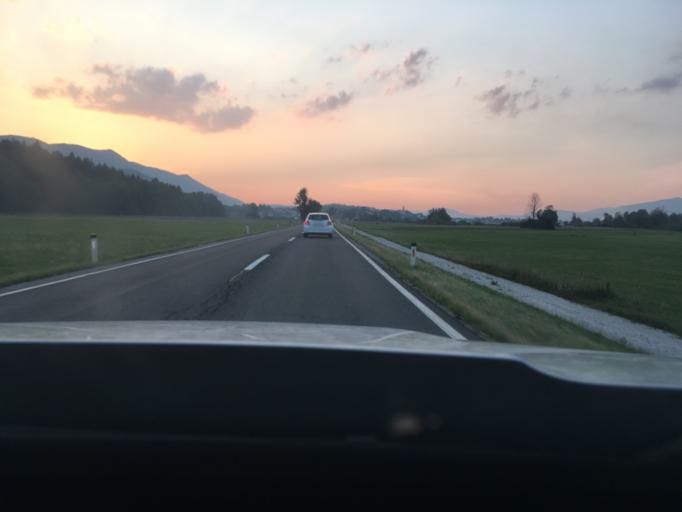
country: SI
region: Ribnica
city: Ribnica
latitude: 45.6949
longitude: 14.7683
